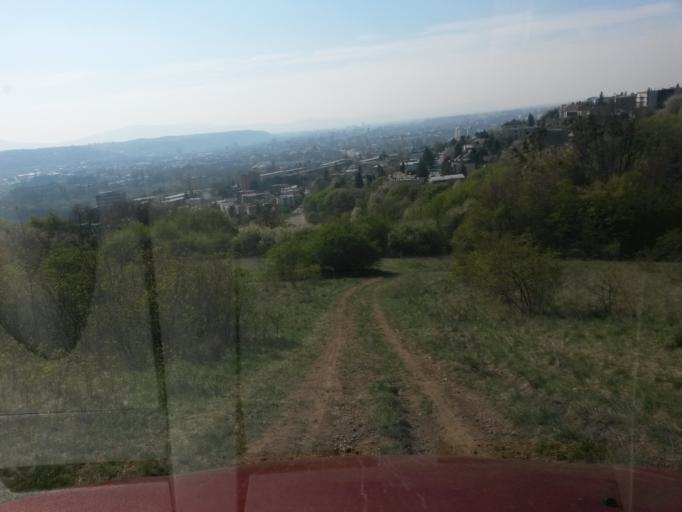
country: SK
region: Kosicky
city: Kosice
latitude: 48.7560
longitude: 21.2403
